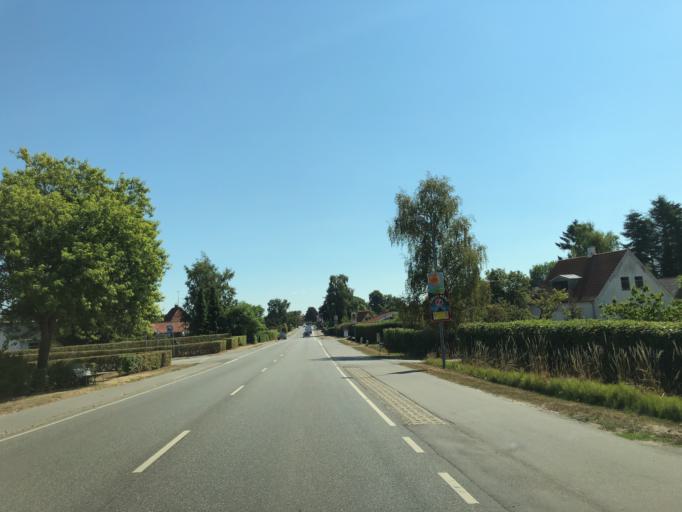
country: DK
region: Zealand
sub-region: Odsherred Kommune
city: Nykobing Sjaelland
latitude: 55.9430
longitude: 11.7449
